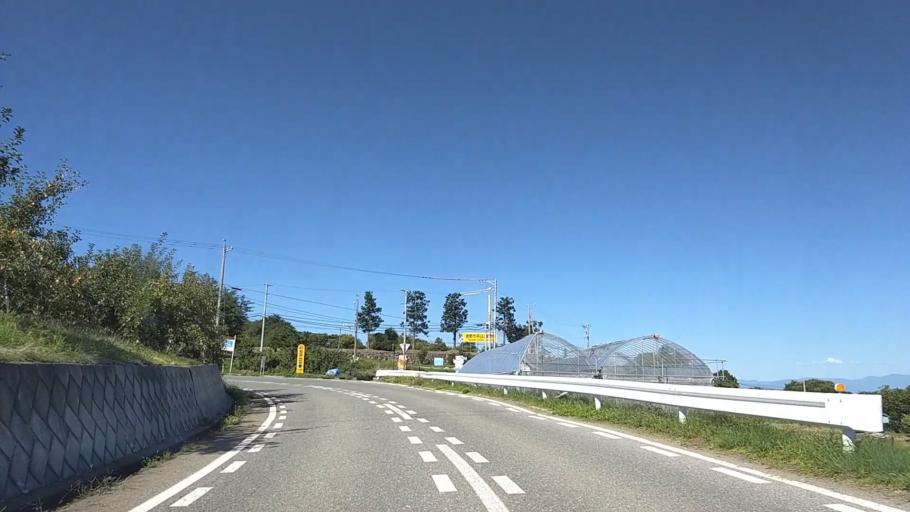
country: JP
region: Nagano
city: Nagano-shi
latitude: 36.5822
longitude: 138.1126
